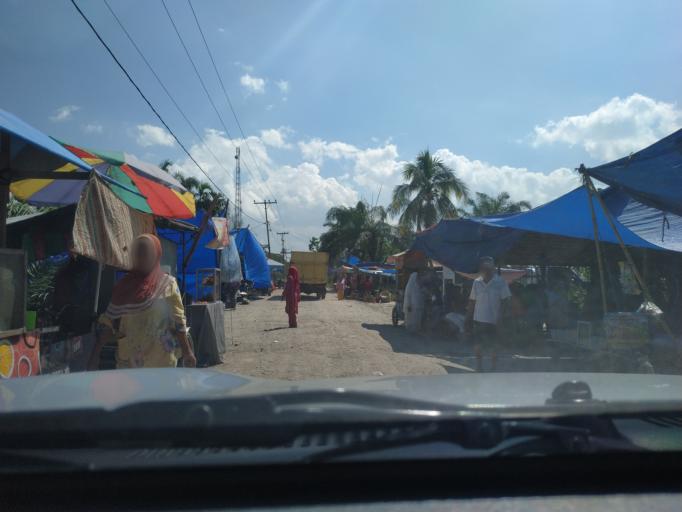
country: ID
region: North Sumatra
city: Tanjungbalai
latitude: 2.8755
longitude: 99.8607
